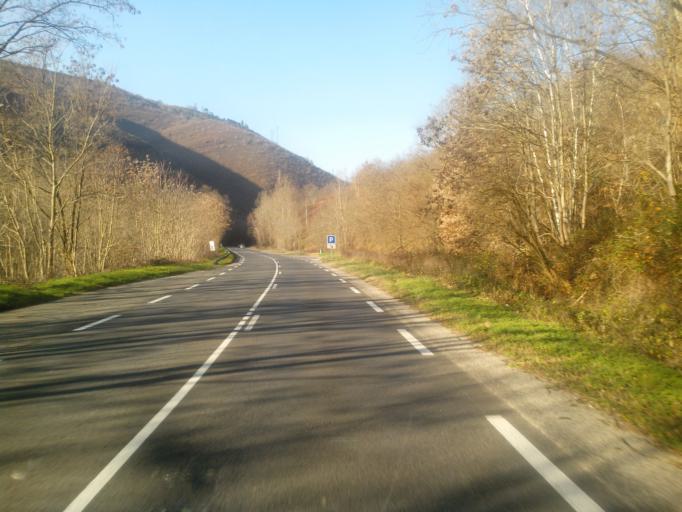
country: FR
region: Midi-Pyrenees
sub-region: Departement de l'Aveyron
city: Viviez
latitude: 44.5668
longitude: 2.2117
